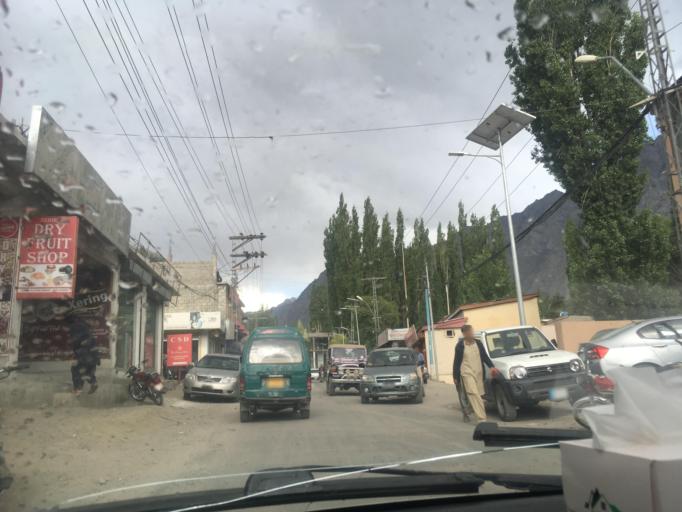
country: PK
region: Gilgit-Baltistan
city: Skardu
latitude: 35.2975
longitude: 75.6413
